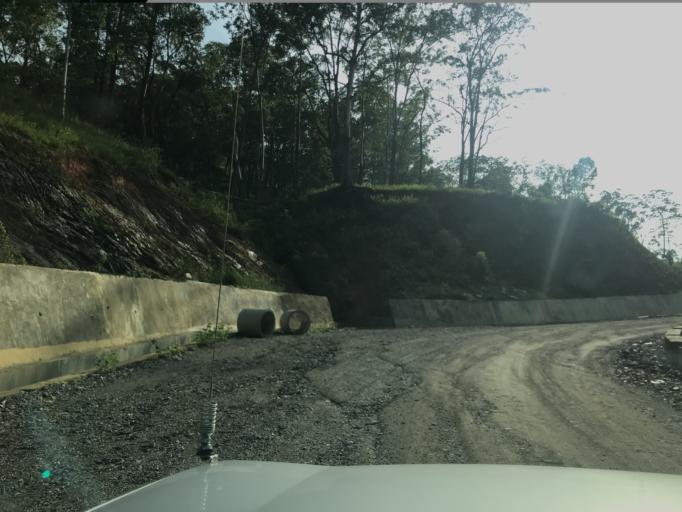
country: TL
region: Aileu
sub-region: Aileu Villa
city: Aileu
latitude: -8.6629
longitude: 125.5331
